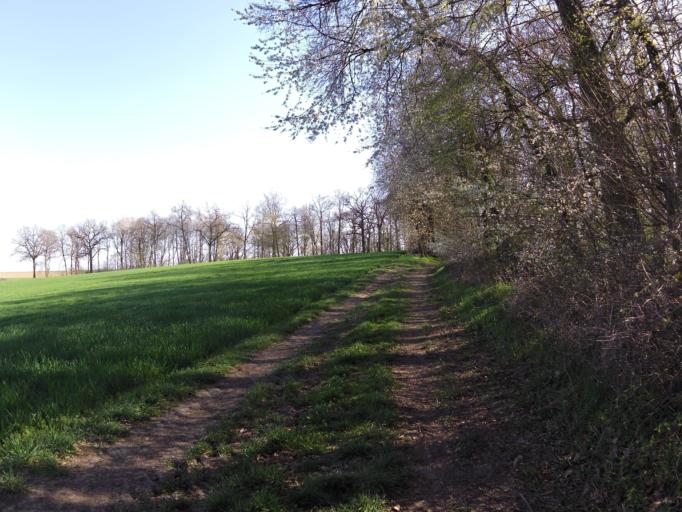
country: DE
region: Bavaria
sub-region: Regierungsbezirk Unterfranken
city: Rottendorf
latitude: 49.8242
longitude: 10.0656
